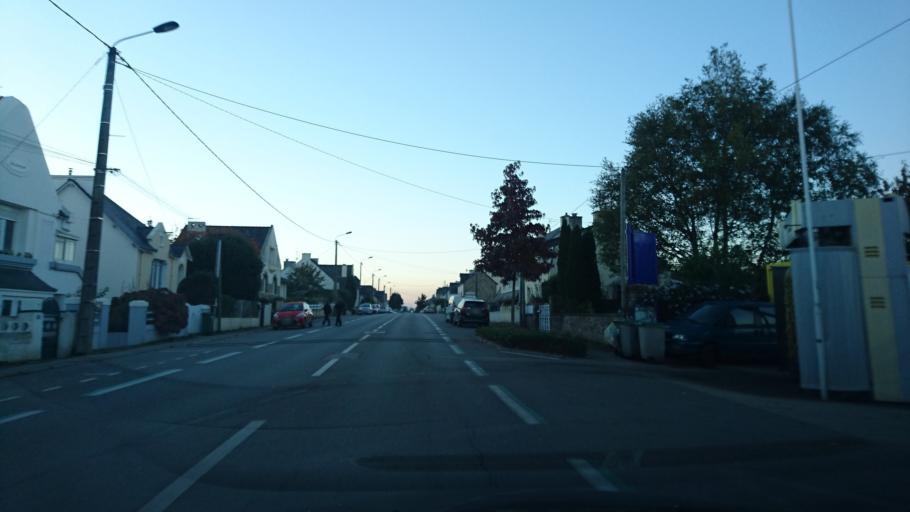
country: FR
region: Brittany
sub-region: Departement du Morbihan
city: Auray
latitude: 47.6745
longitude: -3.0017
